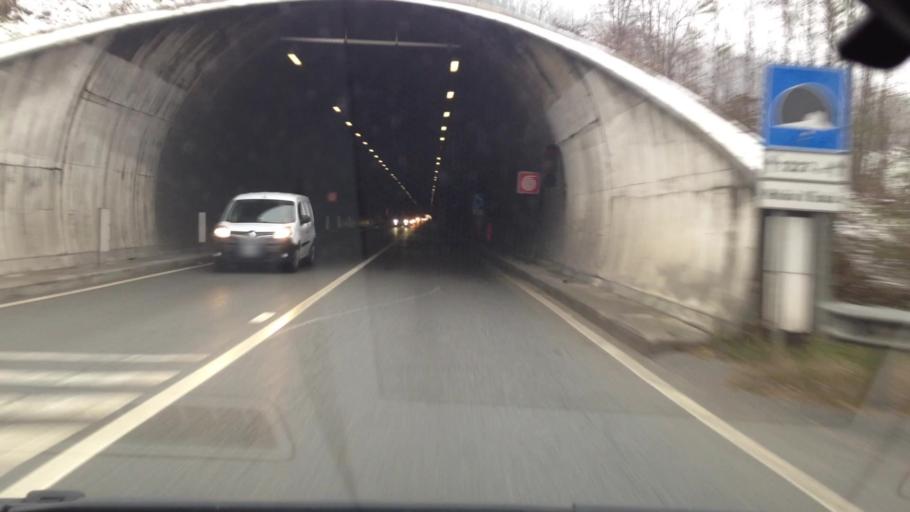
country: IT
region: Piedmont
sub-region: Provincia di Asti
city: Isola d'Asti
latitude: 44.8416
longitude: 8.1932
